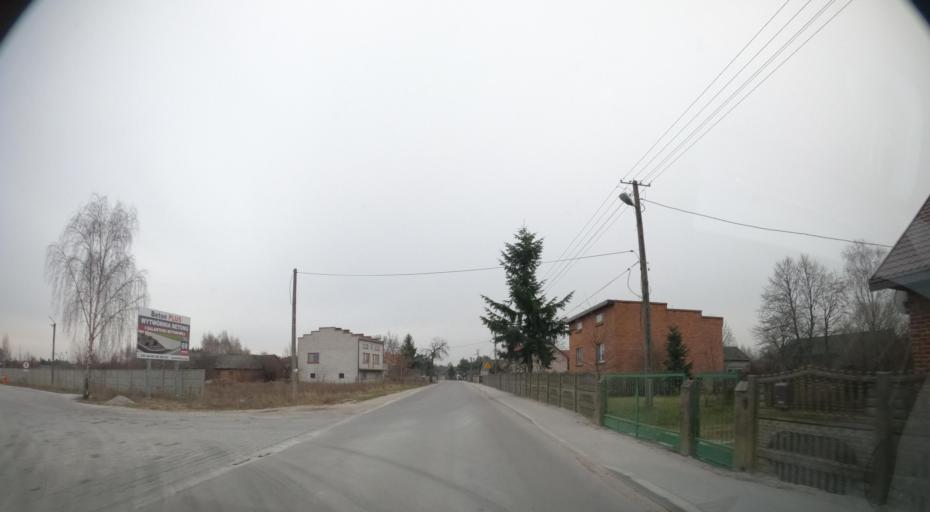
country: PL
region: Masovian Voivodeship
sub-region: Powiat radomski
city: Jastrzebia
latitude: 51.4896
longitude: 21.1853
